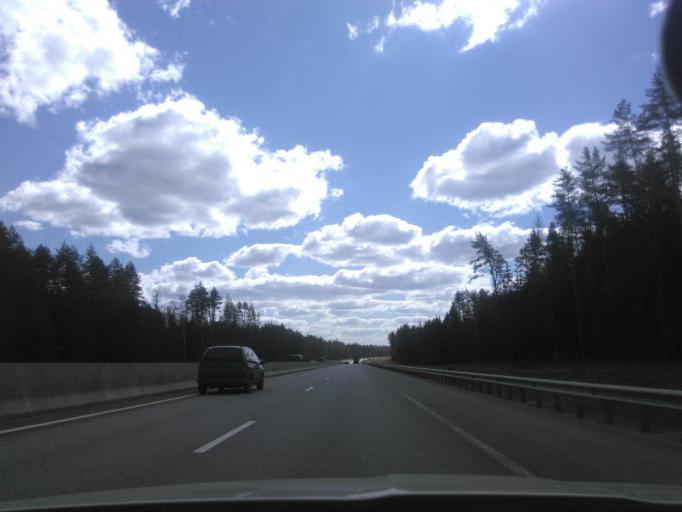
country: RU
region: Moskovskaya
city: Mendeleyevo
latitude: 56.0582
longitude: 37.2458
